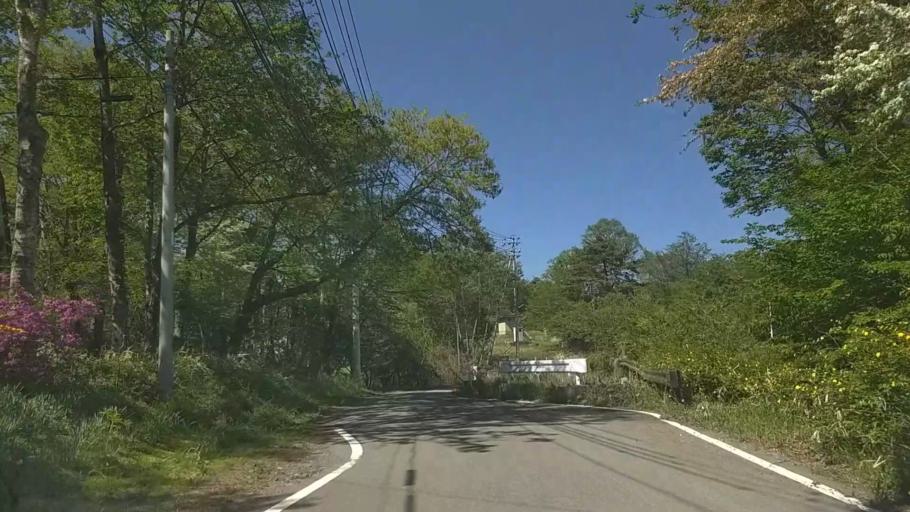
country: JP
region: Yamanashi
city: Nirasaki
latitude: 35.9151
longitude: 138.4323
